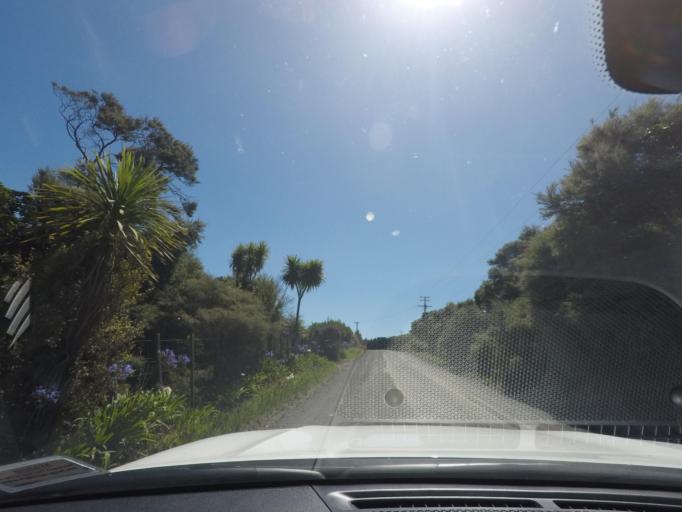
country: NZ
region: Auckland
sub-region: Auckland
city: Parakai
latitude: -36.5831
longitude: 174.3064
